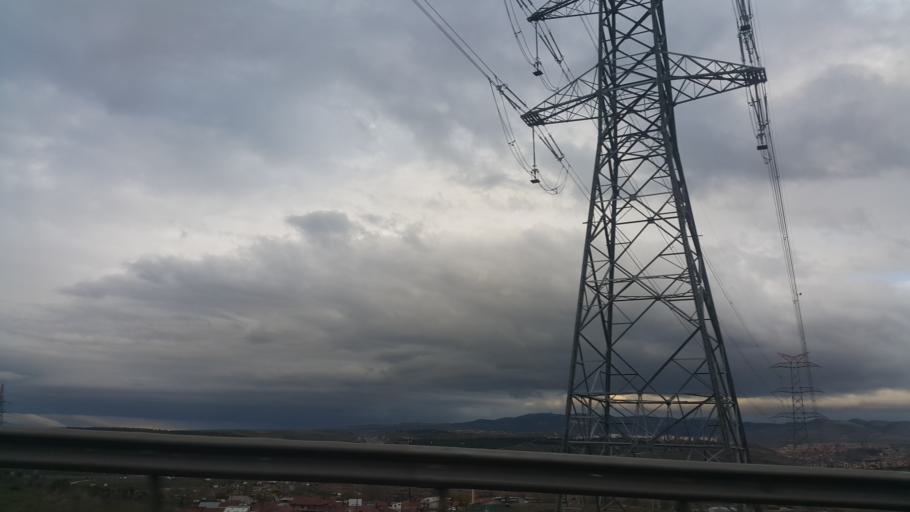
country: TR
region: Ankara
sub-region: Goelbasi
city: Golbasi
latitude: 39.8087
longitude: 32.8011
